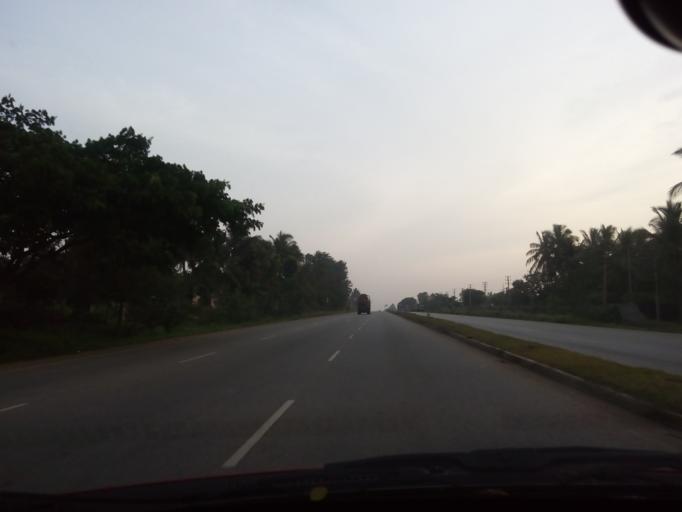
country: IN
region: Karnataka
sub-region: Bangalore Rural
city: Devanhalli
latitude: 13.2795
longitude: 77.7221
